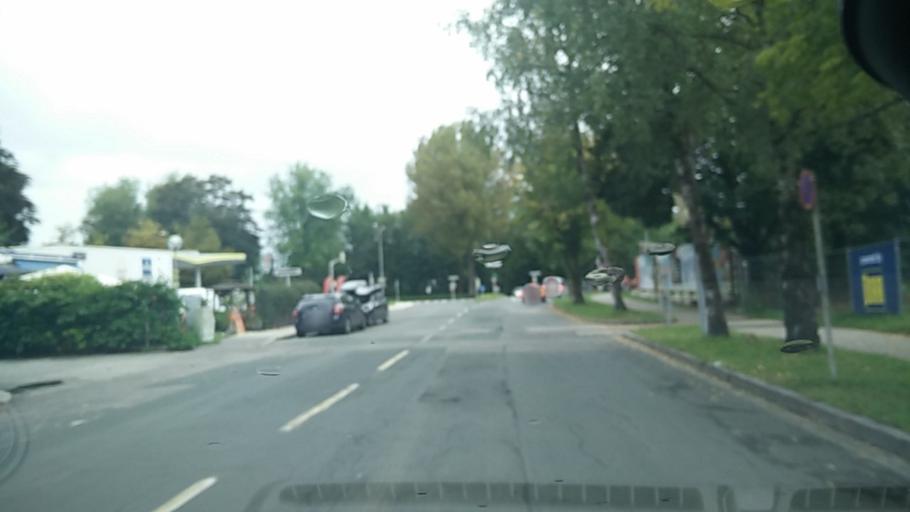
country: AT
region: Carinthia
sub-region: Klagenfurt am Woerthersee
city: Klagenfurt am Woerthersee
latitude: 46.6211
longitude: 14.2686
